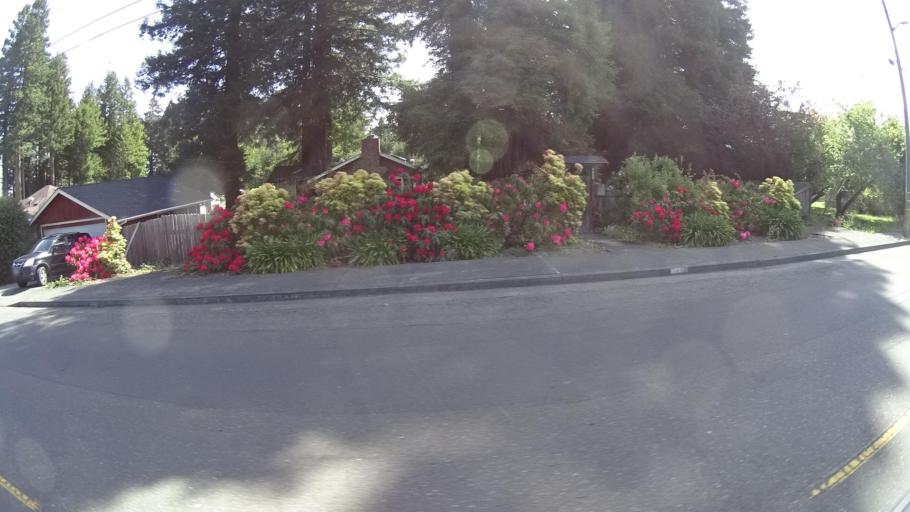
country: US
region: California
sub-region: Humboldt County
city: Cutten
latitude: 40.7771
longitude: -124.1397
